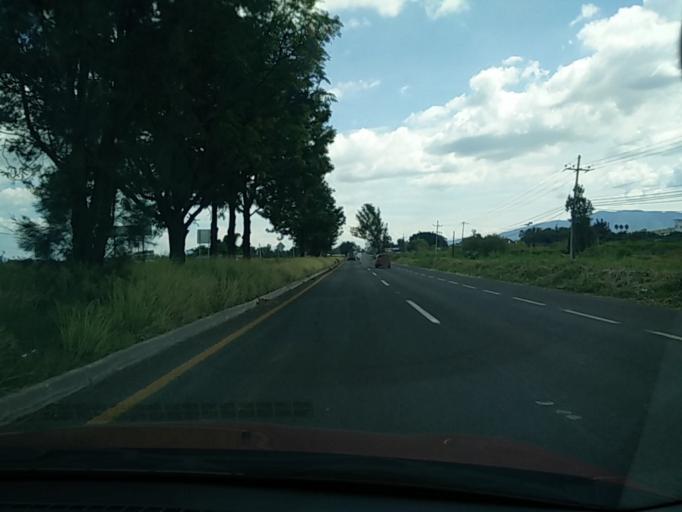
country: MX
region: Jalisco
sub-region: Tlajomulco de Zuniga
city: Rancho Alegre [Fraccionamiento]
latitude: 20.4624
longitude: -103.2555
